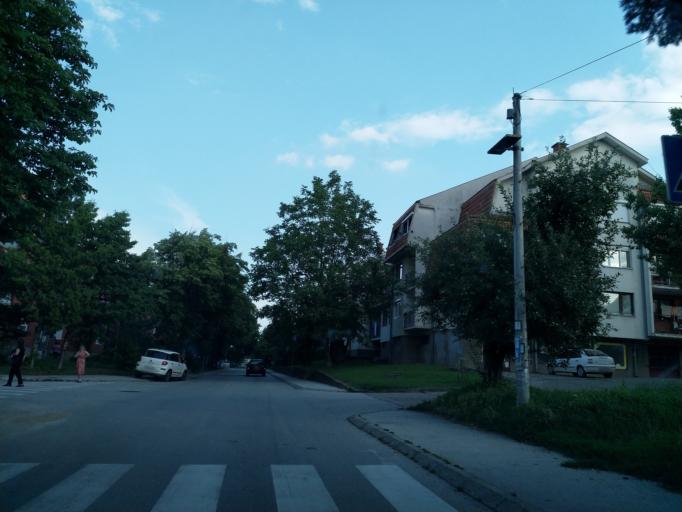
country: RS
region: Central Serbia
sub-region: Pomoravski Okrug
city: Jagodina
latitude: 43.9799
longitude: 21.2463
